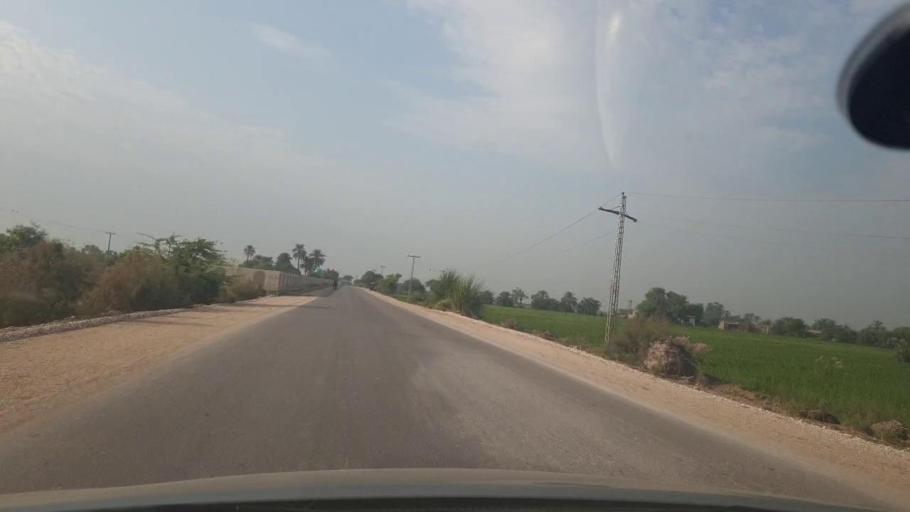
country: PK
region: Sindh
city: Jacobabad
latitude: 28.1954
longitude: 68.3677
